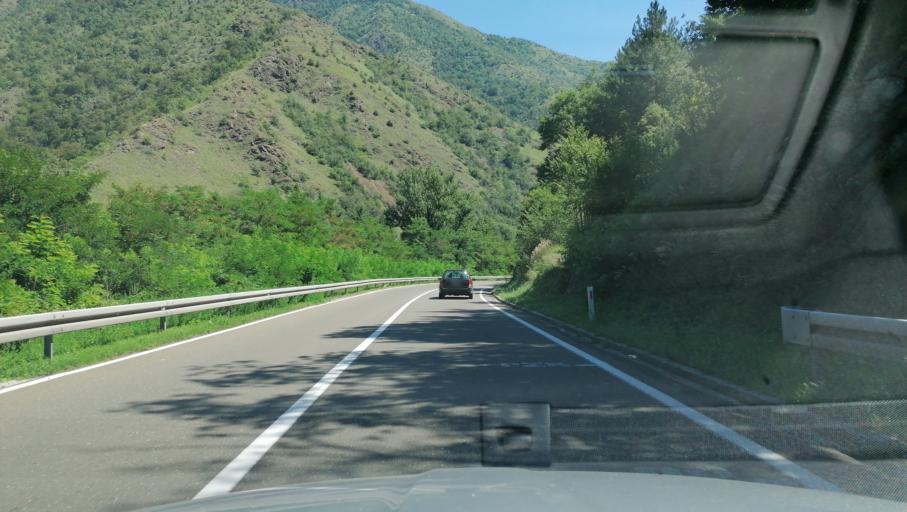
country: RS
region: Central Serbia
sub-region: Raski Okrug
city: Kraljevo
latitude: 43.5817
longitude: 20.5823
